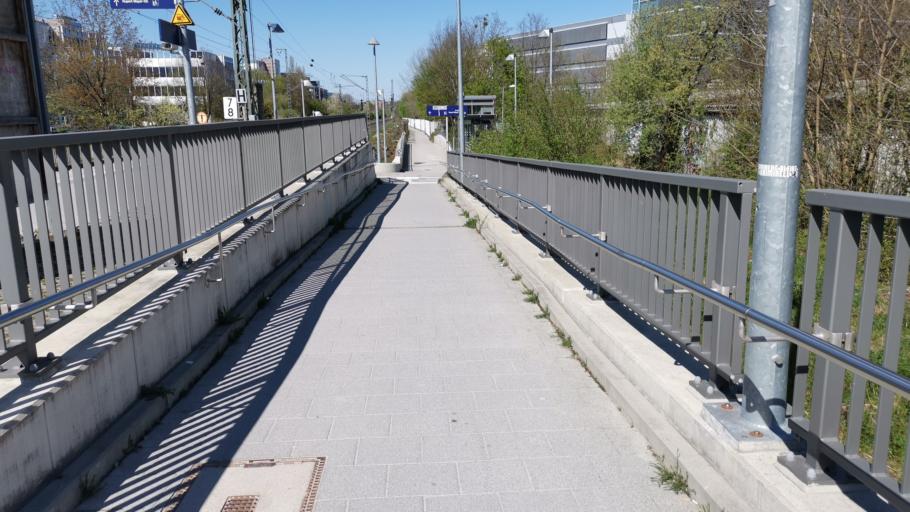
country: DE
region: Bavaria
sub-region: Upper Bavaria
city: Pullach im Isartal
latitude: 48.0952
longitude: 11.5333
